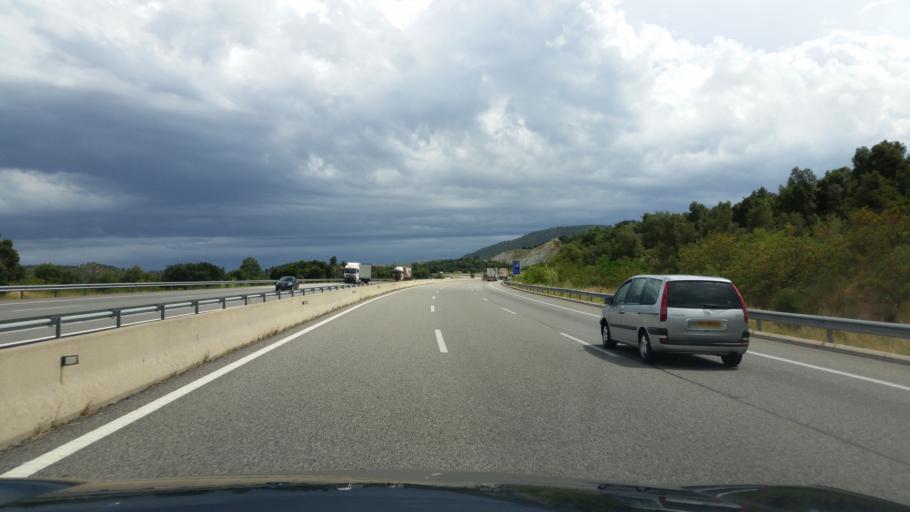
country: ES
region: Catalonia
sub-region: Provincia de Girona
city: Capmany
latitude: 42.3821
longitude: 2.8855
